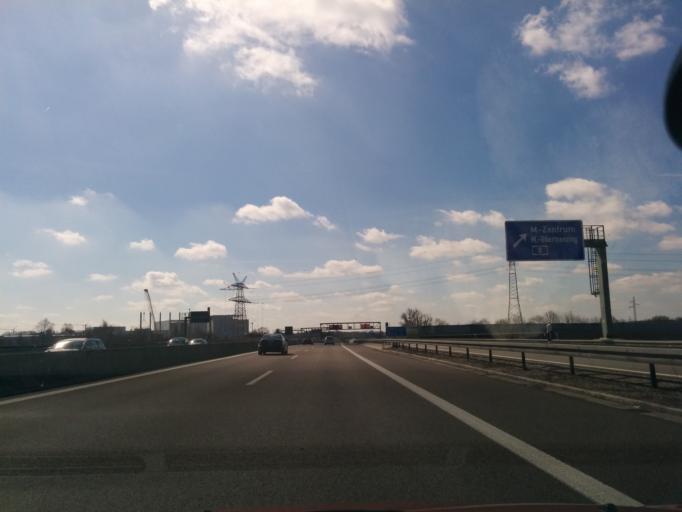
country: DE
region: Bavaria
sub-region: Upper Bavaria
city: Pasing
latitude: 48.1820
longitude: 11.4331
